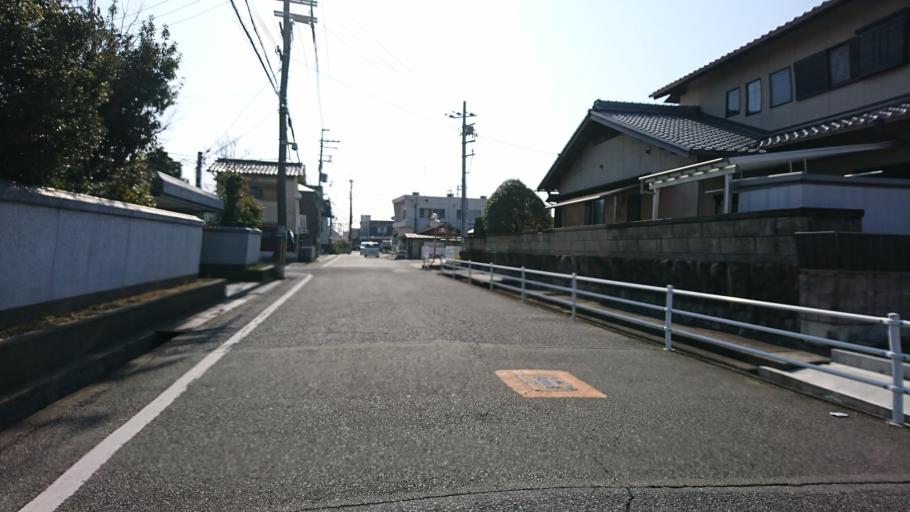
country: JP
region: Hyogo
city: Kakogawacho-honmachi
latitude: 34.7562
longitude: 134.8212
